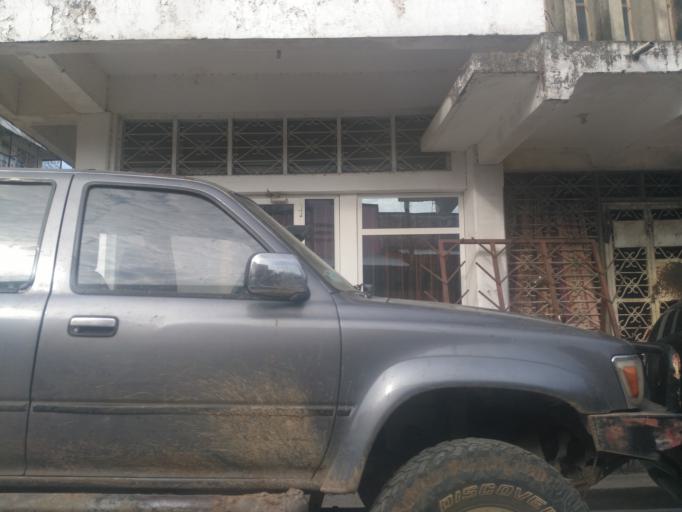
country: TZ
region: Zanzibar Urban/West
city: Zanzibar
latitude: -6.1600
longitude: 39.2002
